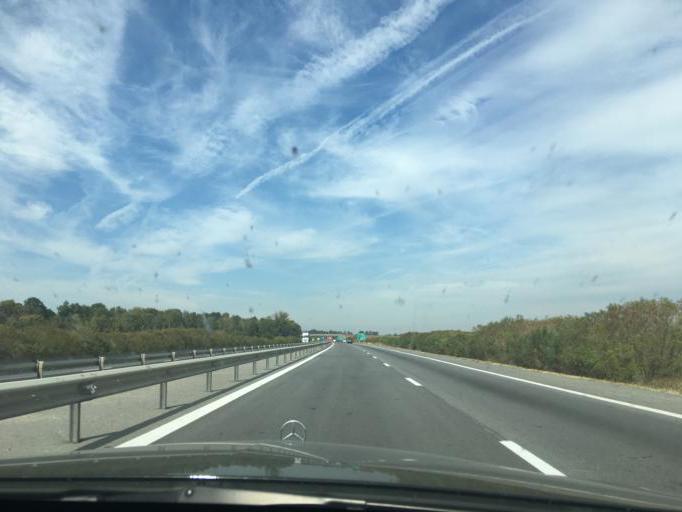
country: RO
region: Dambovita
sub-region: Comuna Corbii Mari
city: Grozavesti
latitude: 44.5977
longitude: 25.4598
